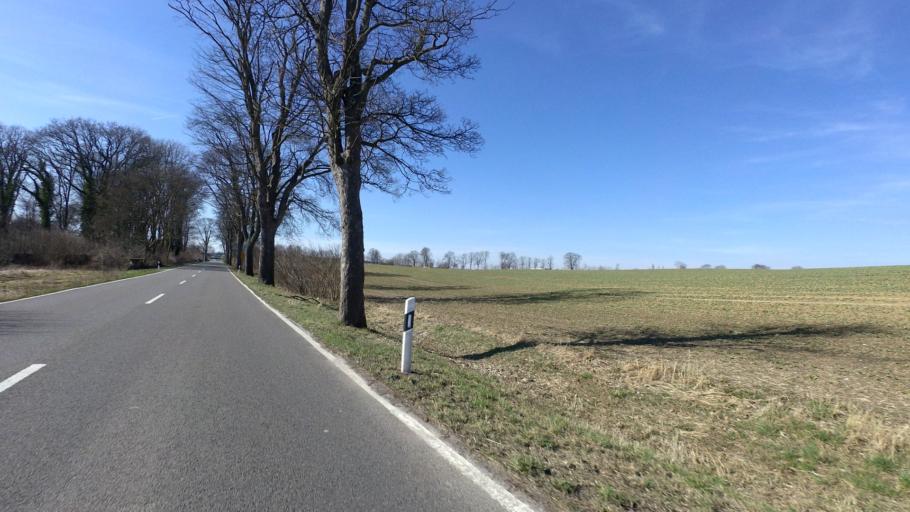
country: DE
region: Brandenburg
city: Protzel
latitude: 52.6366
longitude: 13.9973
